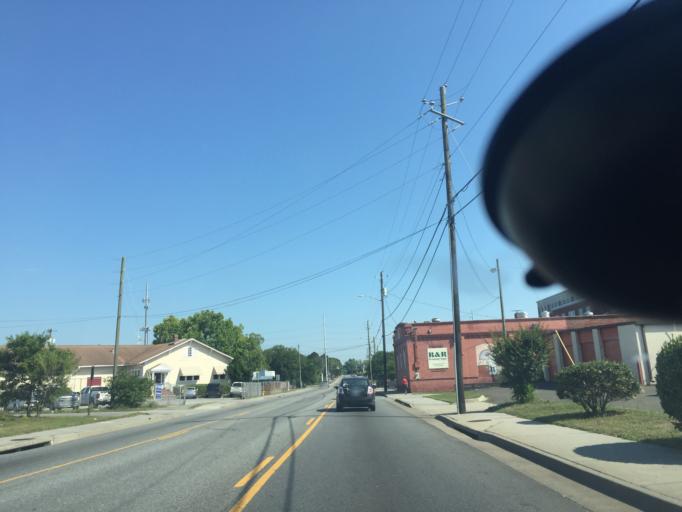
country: US
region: Georgia
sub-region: Chatham County
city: Savannah
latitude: 32.0713
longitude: -81.0833
